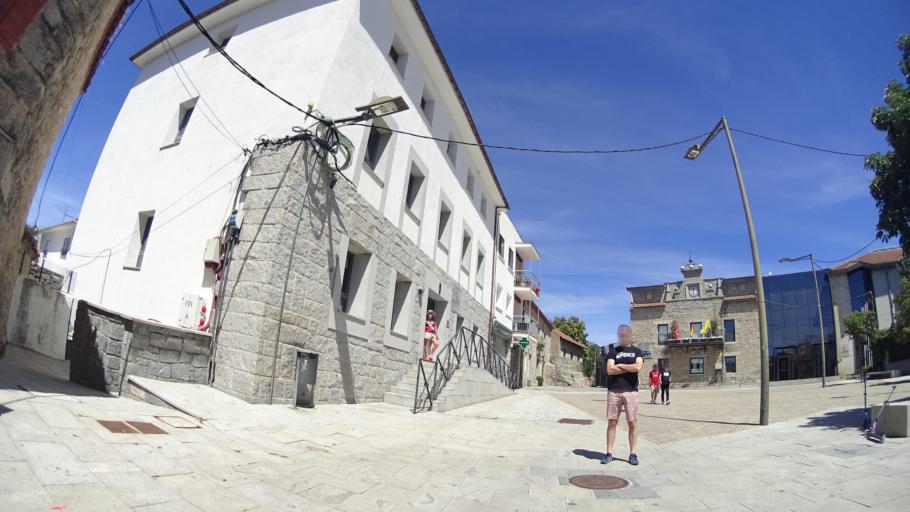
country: ES
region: Madrid
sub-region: Provincia de Madrid
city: Collado-Villalba
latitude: 40.6453
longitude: -3.9918
